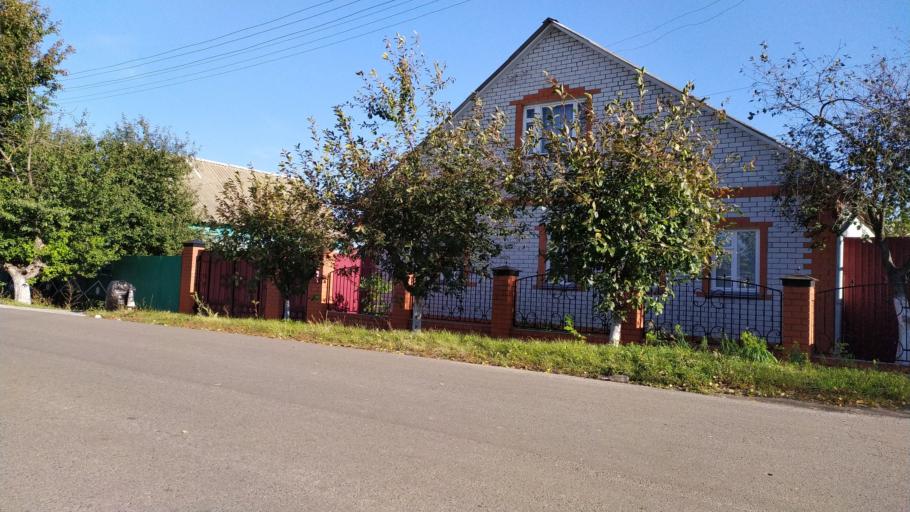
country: RU
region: Kursk
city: Kursk
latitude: 51.6425
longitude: 36.1412
